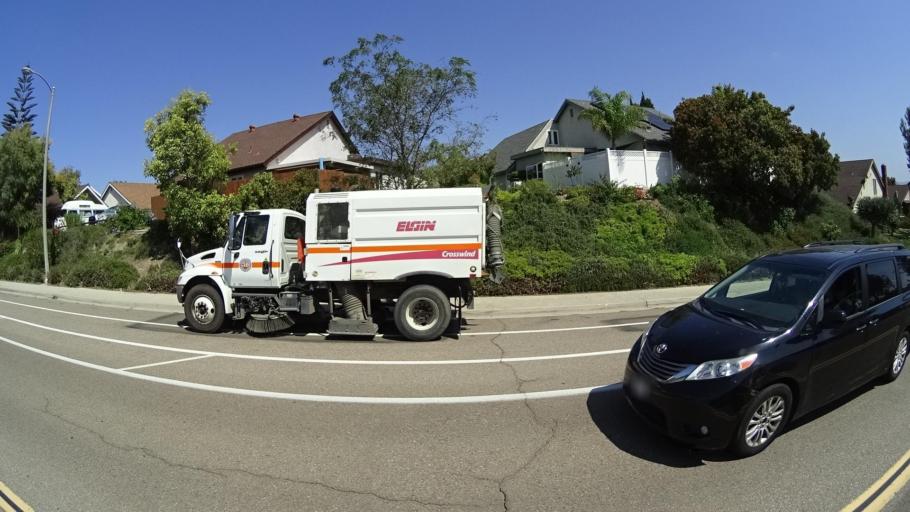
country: US
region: California
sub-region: San Diego County
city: Spring Valley
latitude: 32.7321
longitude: -116.9837
